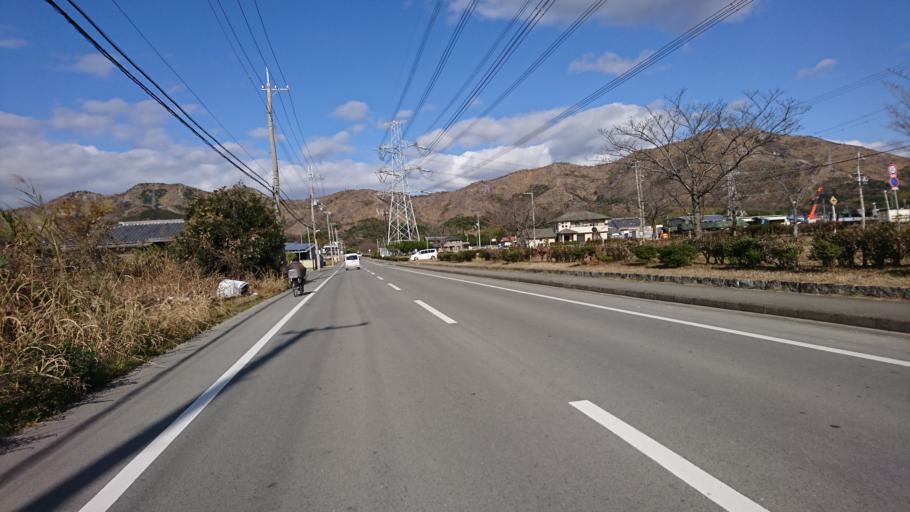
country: JP
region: Hyogo
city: Kakogawacho-honmachi
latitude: 34.8003
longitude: 134.7832
